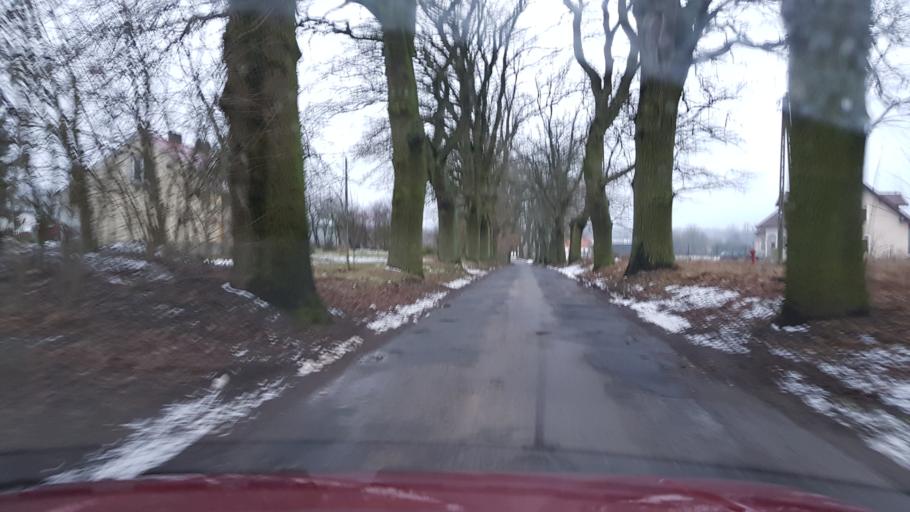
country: PL
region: West Pomeranian Voivodeship
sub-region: Powiat goleniowski
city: Mosty
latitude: 53.5027
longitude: 14.9175
